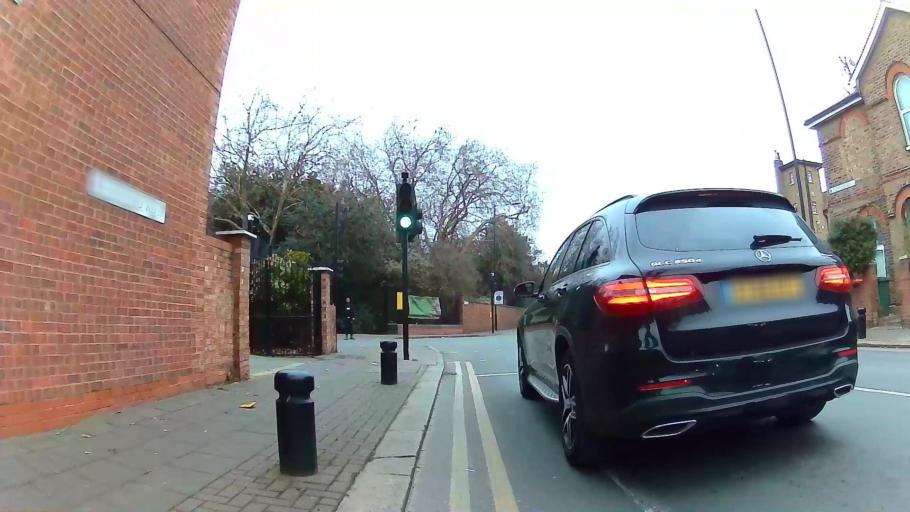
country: GB
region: England
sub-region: Greater London
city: East Ham
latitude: 51.5367
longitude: 0.0220
